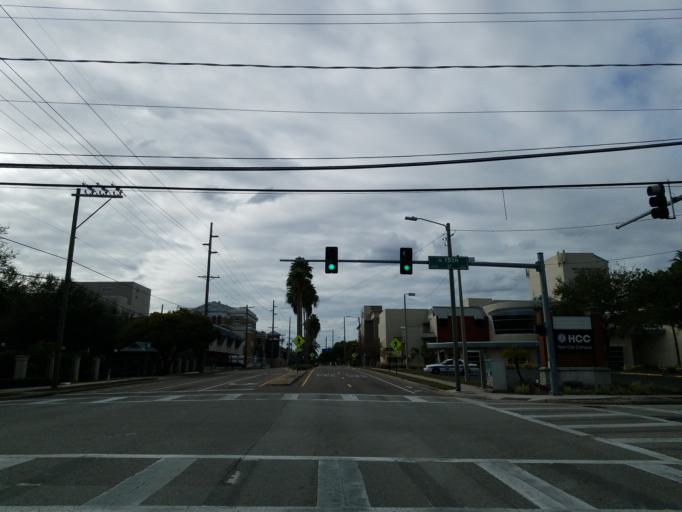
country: US
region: Florida
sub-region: Hillsborough County
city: Tampa
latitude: 27.9625
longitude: -82.4428
